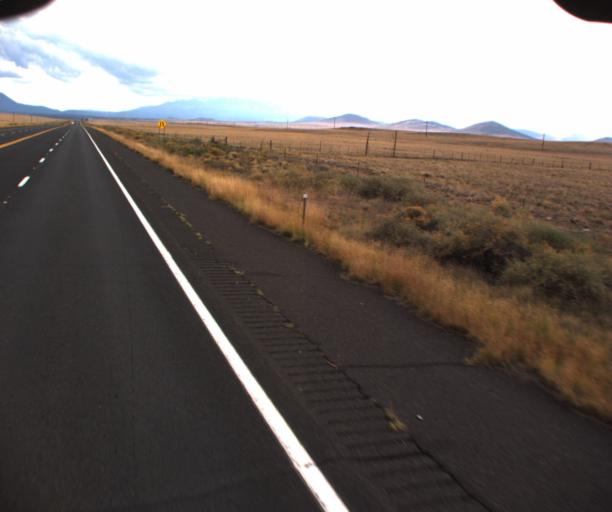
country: US
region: Arizona
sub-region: Coconino County
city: Flagstaff
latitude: 35.6252
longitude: -111.5212
